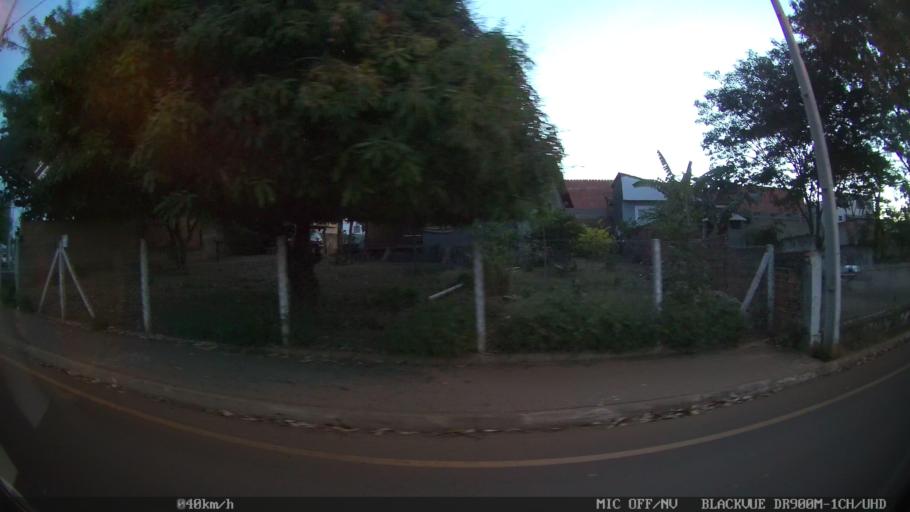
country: BR
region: Sao Paulo
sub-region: Catanduva
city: Catanduva
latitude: -21.1372
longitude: -48.9896
